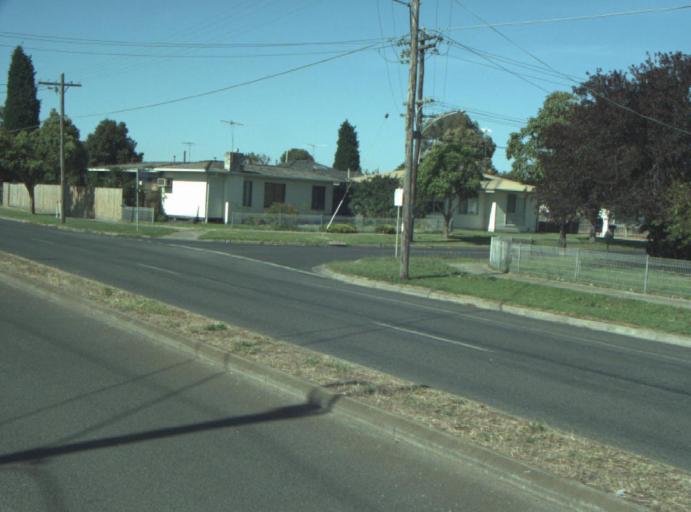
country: AU
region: Victoria
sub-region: Greater Geelong
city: Bell Park
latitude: -38.0884
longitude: 144.3668
